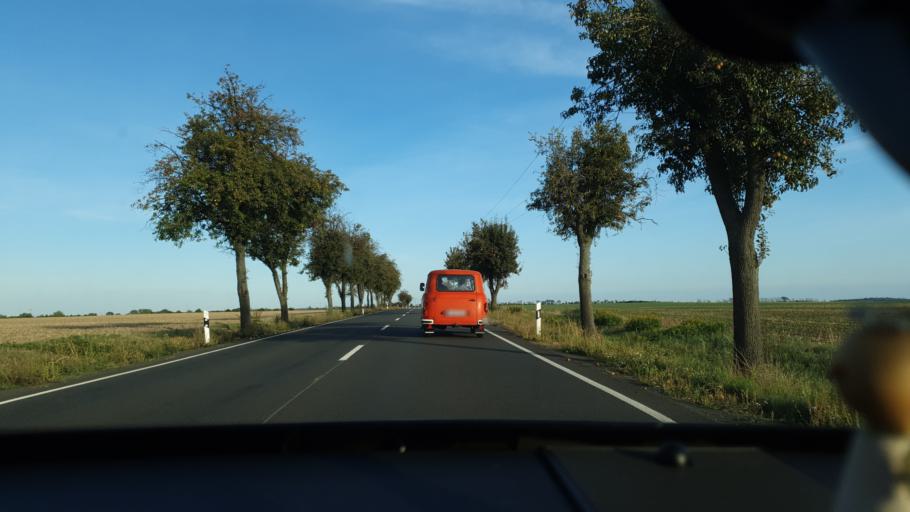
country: DE
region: Saxony
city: Krostitz
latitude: 51.4595
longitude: 12.4766
